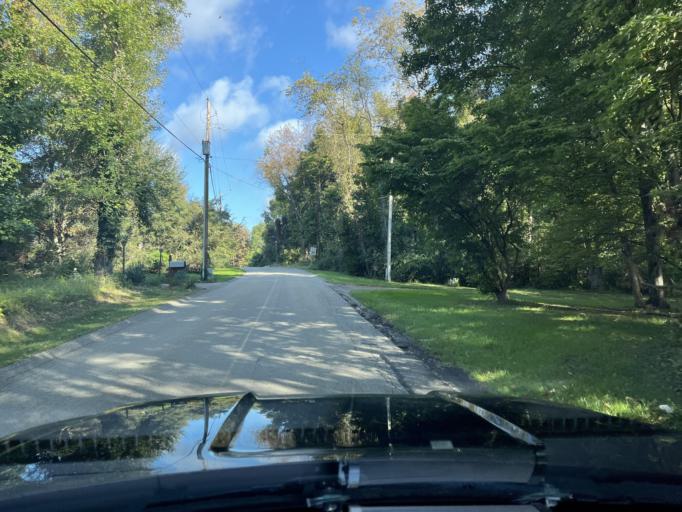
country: US
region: Pennsylvania
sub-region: Fayette County
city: South Uniontown
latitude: 39.8875
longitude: -79.7558
